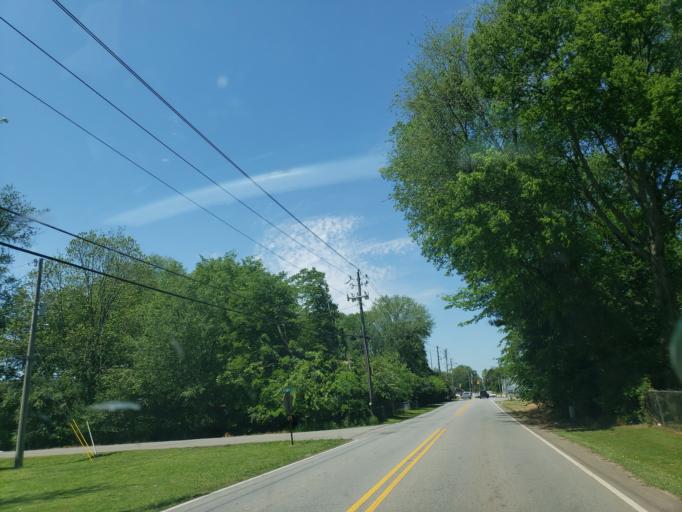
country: US
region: Alabama
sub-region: Madison County
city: Hazel Green
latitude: 34.9322
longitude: -86.5694
